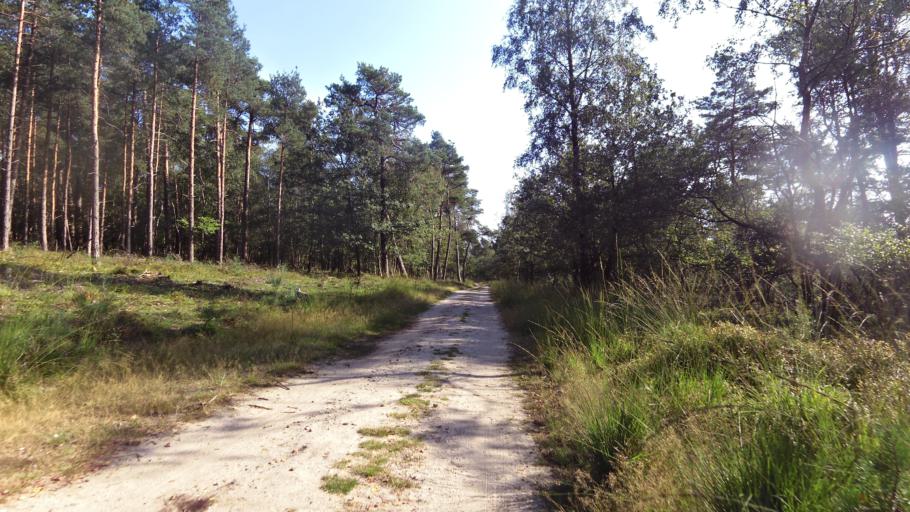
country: NL
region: Gelderland
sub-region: Gemeente Apeldoorn
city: Beekbergen
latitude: 52.1219
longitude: 5.9347
